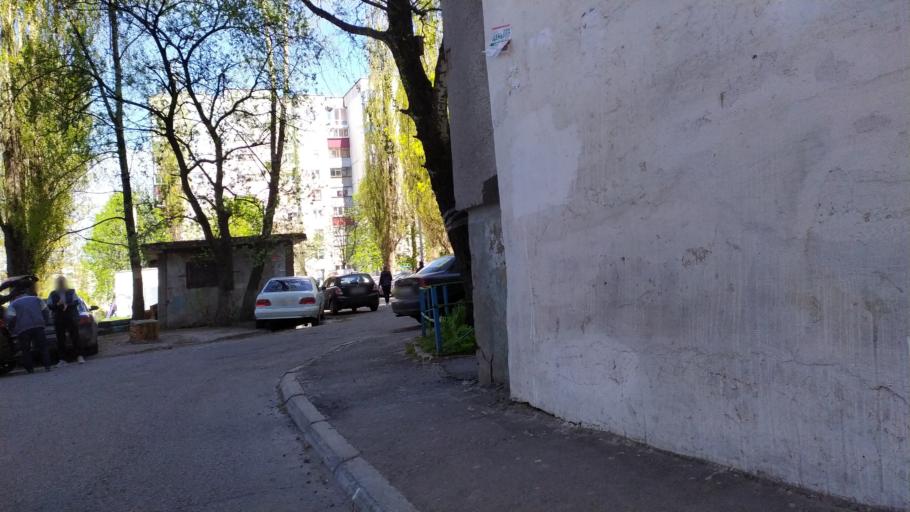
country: RU
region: Kursk
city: Kursk
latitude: 51.7447
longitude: 36.1339
